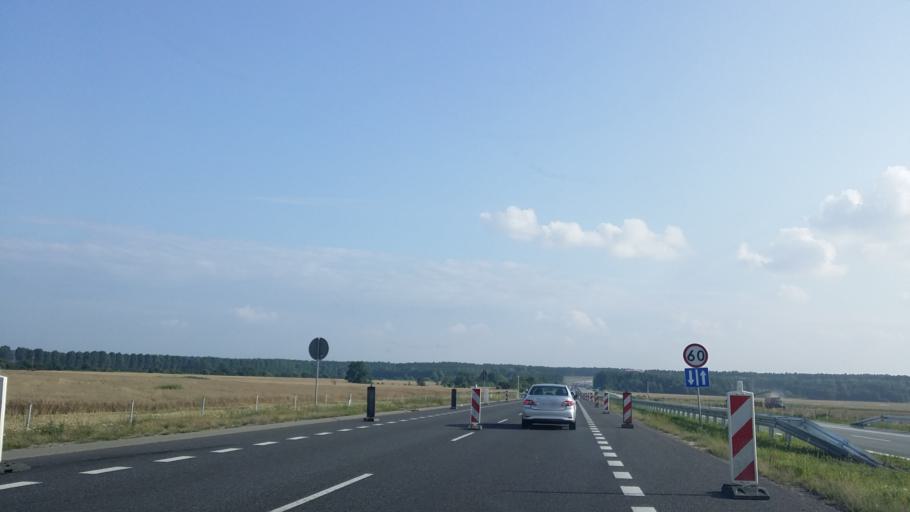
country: PL
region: Lubusz
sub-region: Powiat miedzyrzecki
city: Miedzyrzecz
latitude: 52.4348
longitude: 15.5561
